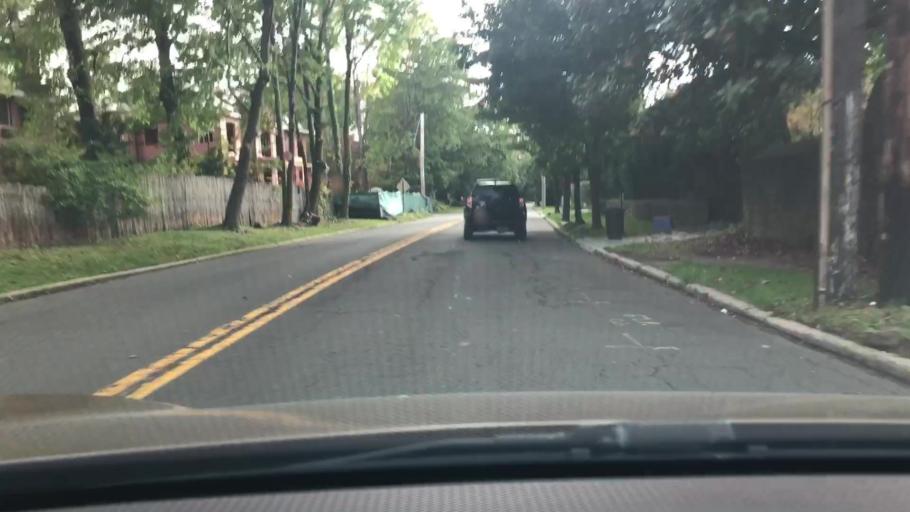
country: US
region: New York
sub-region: Westchester County
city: Bronxville
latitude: 40.9346
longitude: -73.8184
